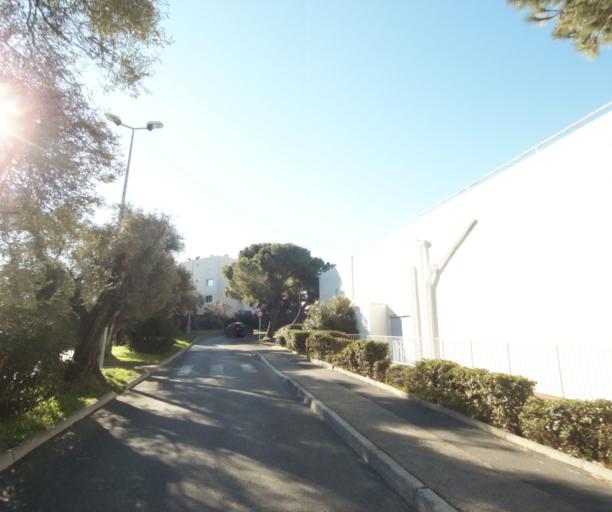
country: FR
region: Provence-Alpes-Cote d'Azur
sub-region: Departement des Alpes-Maritimes
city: Antibes
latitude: 43.5772
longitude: 7.1071
